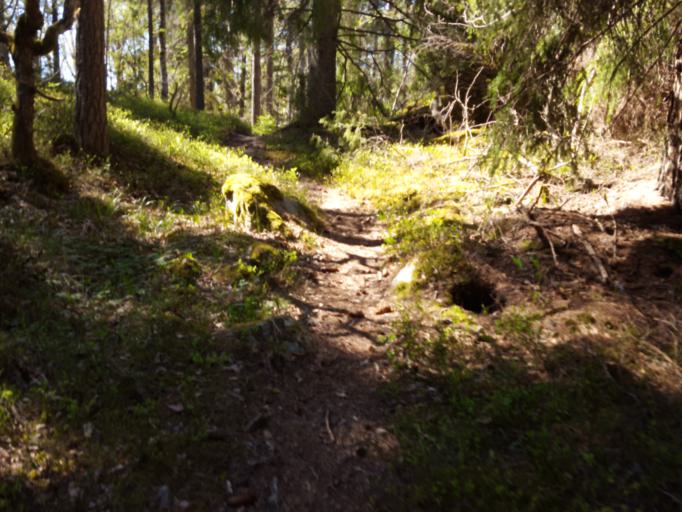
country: SE
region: Uppsala
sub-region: Uppsala Kommun
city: Storvreta
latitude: 59.9036
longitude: 17.7486
